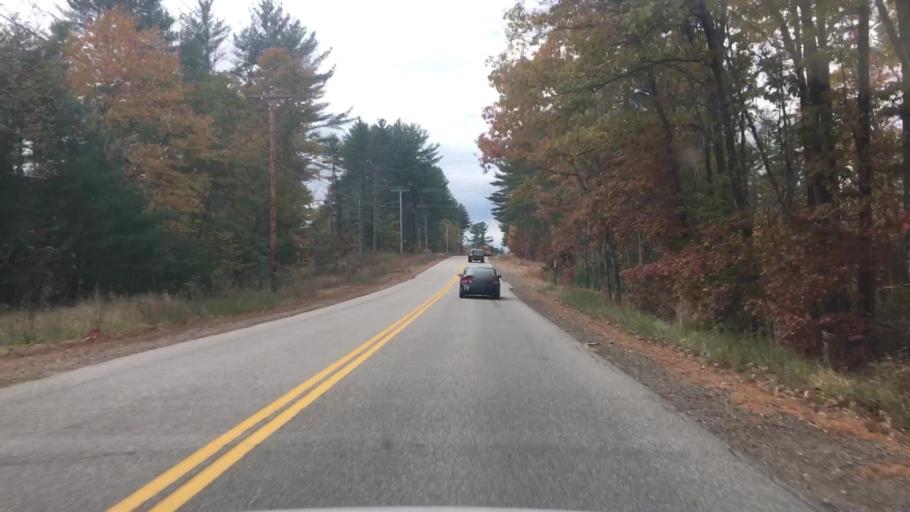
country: US
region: Maine
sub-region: York County
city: Sanford (historical)
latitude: 43.4585
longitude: -70.7760
